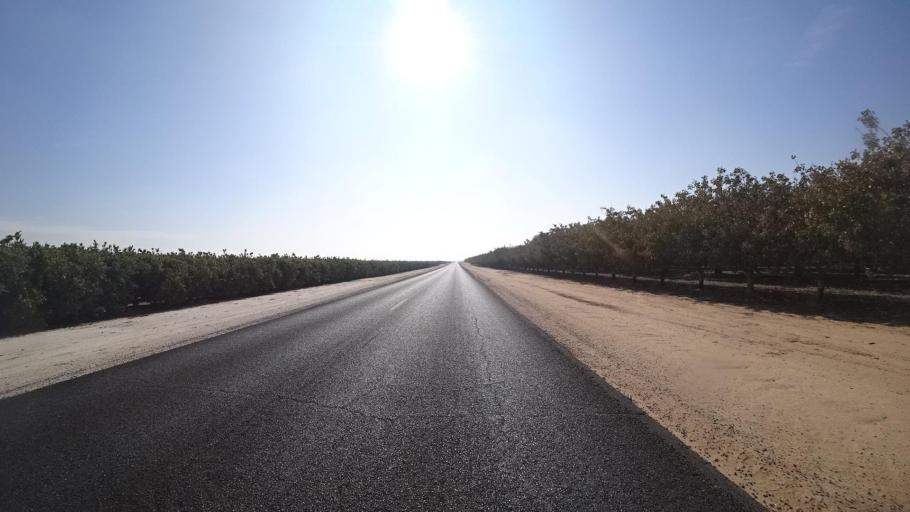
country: US
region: California
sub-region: Kern County
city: McFarland
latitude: 35.5776
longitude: -119.1512
